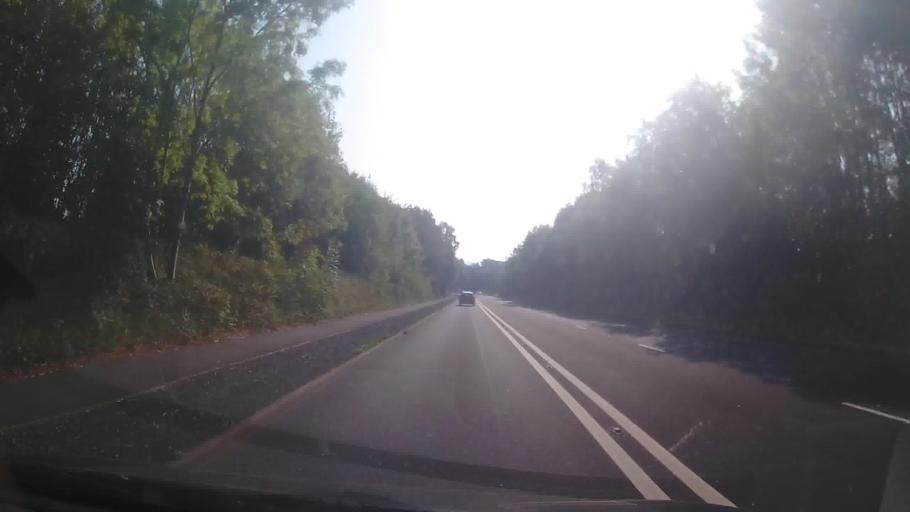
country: GB
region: England
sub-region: Shropshire
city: Bridgnorth
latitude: 52.5305
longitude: -2.4332
